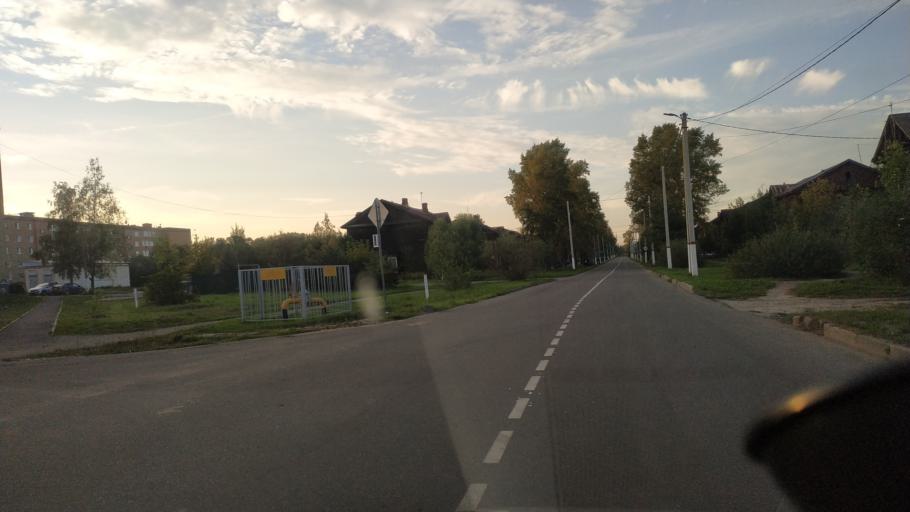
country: RU
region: Moskovskaya
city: Roshal'
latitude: 55.6665
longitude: 39.8525
